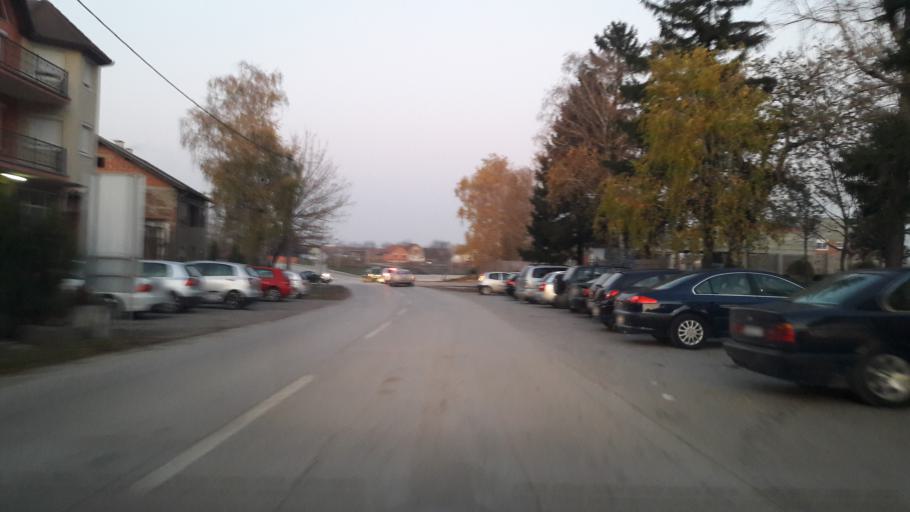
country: HR
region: Vukovarsko-Srijemska
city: Nijemci
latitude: 45.1404
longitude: 19.0358
